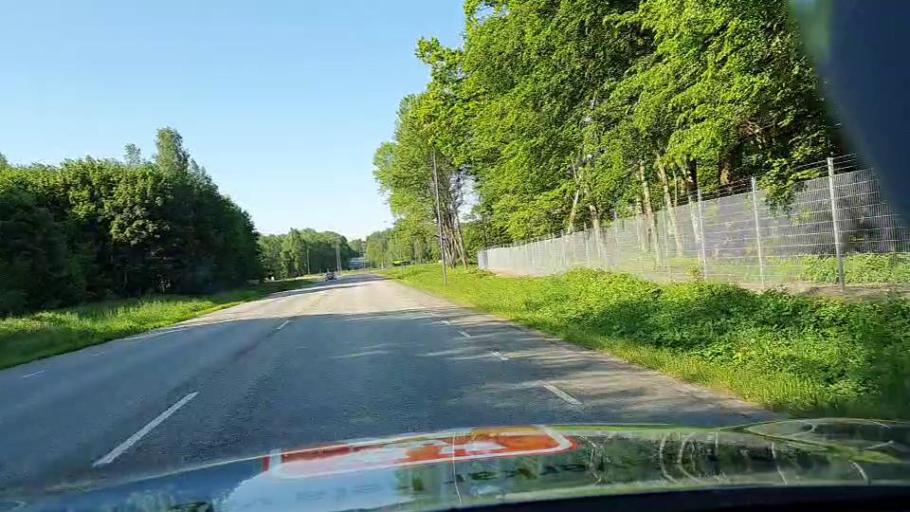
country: SE
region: Skane
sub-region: Hassleholms Kommun
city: Tormestorp
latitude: 56.1357
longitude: 13.7389
